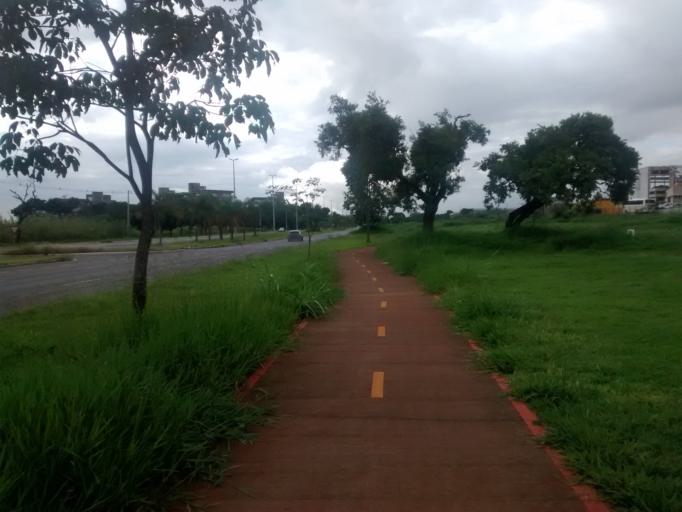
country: BR
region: Federal District
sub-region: Brasilia
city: Brasilia
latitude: -15.7520
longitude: -47.8780
